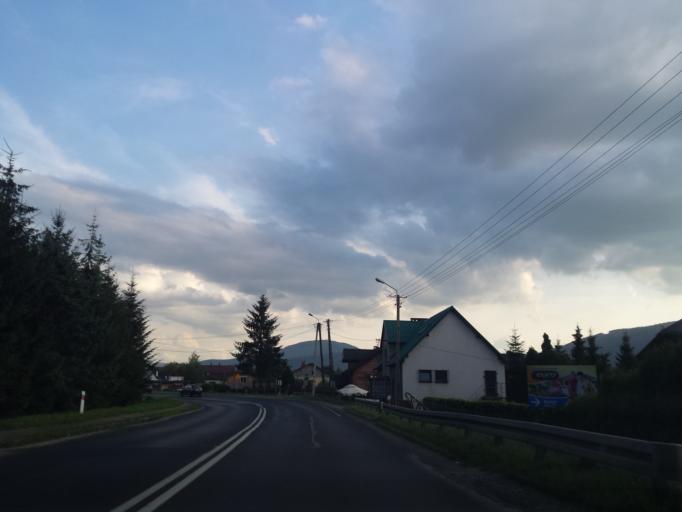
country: PL
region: Silesian Voivodeship
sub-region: Powiat bielski
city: Wilkowice
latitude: 49.7640
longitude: 19.0904
